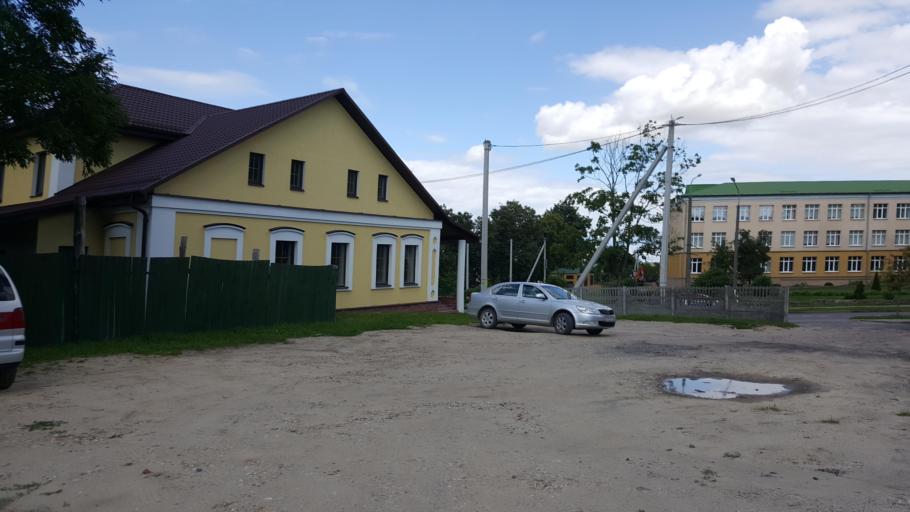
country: BY
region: Brest
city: Kamyanyets
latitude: 52.4030
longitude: 23.8196
